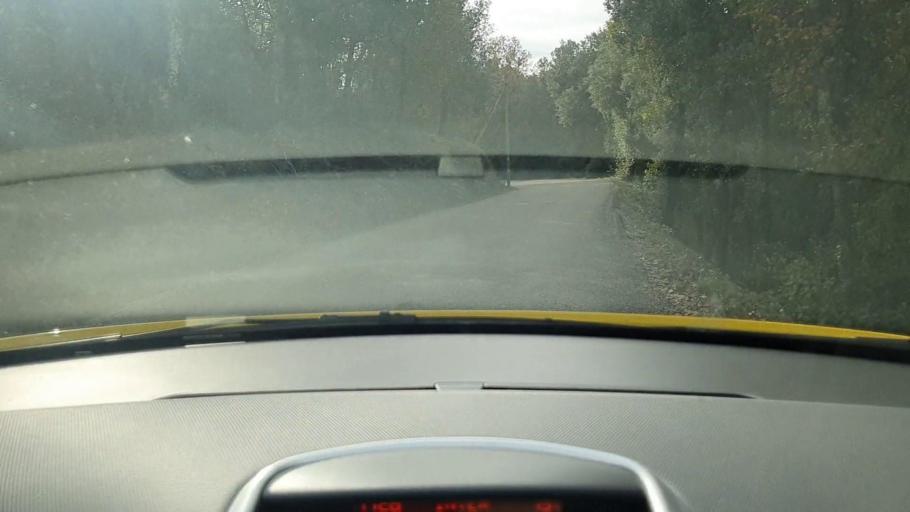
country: FR
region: Languedoc-Roussillon
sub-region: Departement du Gard
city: Anduze
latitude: 44.0452
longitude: 3.9213
